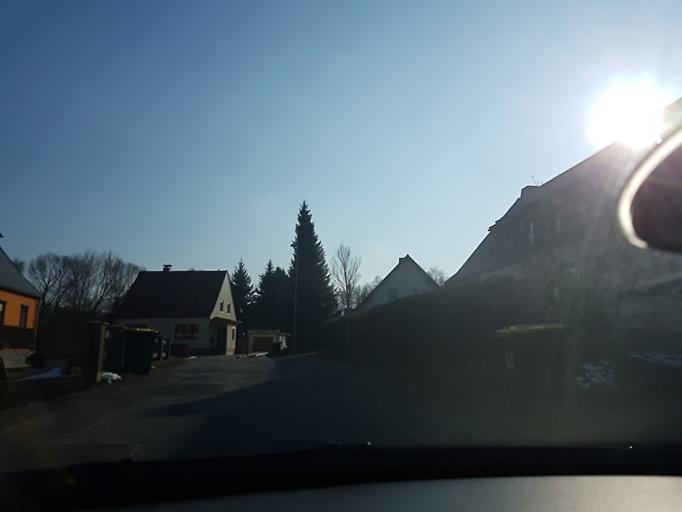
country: DE
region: Saxony
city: Oberschona
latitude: 50.9200
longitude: 13.3003
